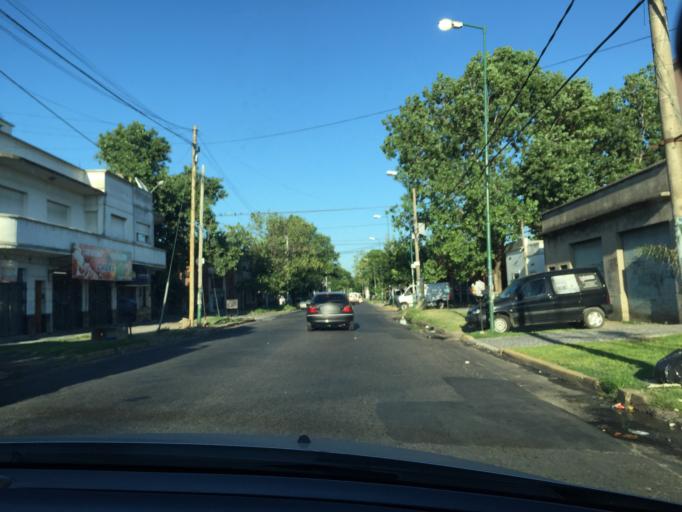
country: AR
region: Buenos Aires
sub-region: Partido de Lomas de Zamora
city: Lomas de Zamora
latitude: -34.7426
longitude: -58.4146
